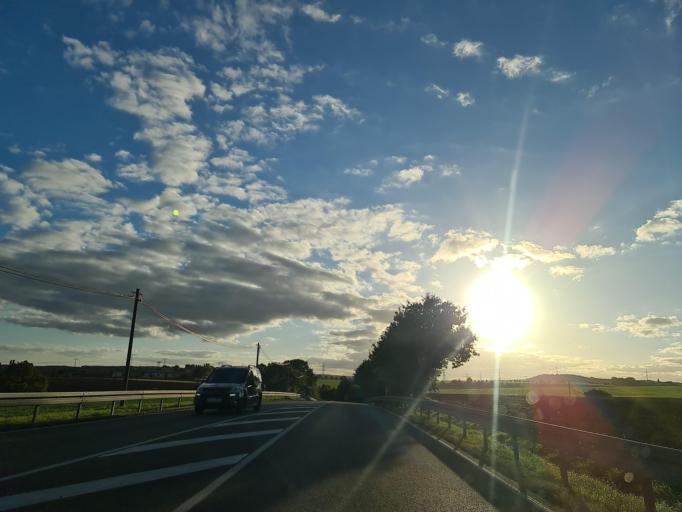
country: DE
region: Thuringia
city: Crimla
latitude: 50.8063
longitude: 12.0713
